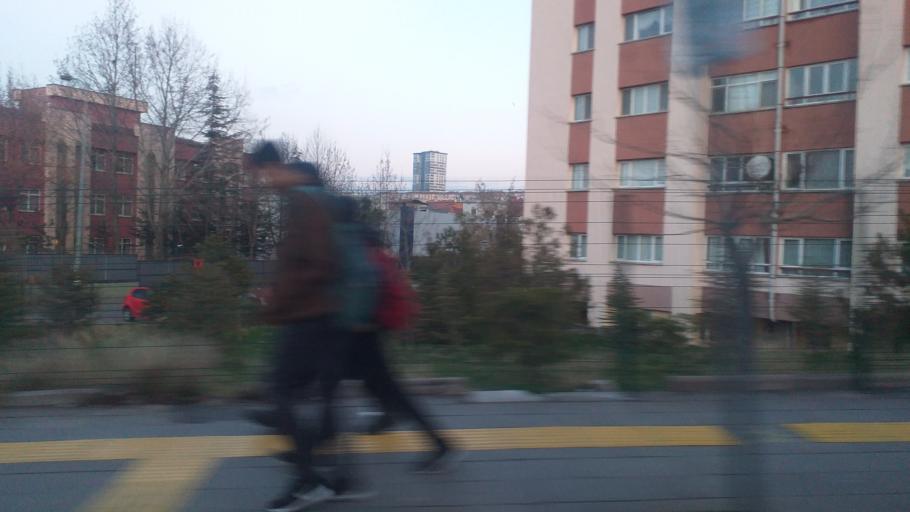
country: TR
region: Ankara
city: Ankara
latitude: 39.9703
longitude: 32.8427
